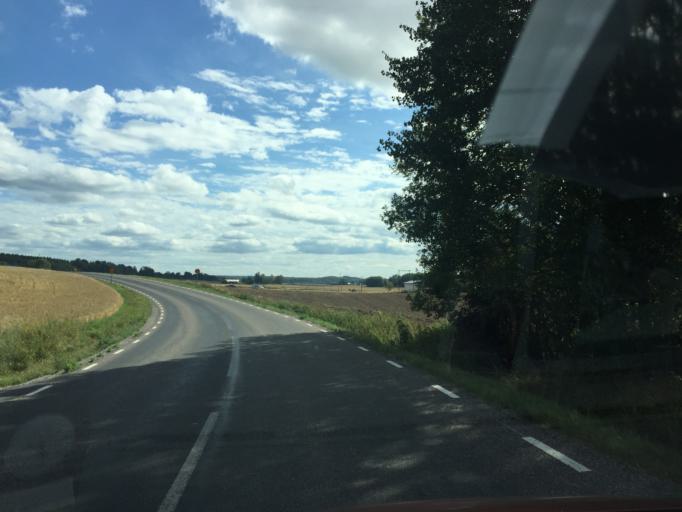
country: SE
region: OErebro
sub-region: Hallsbergs Kommun
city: Hallsberg
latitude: 59.1138
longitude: 15.0091
